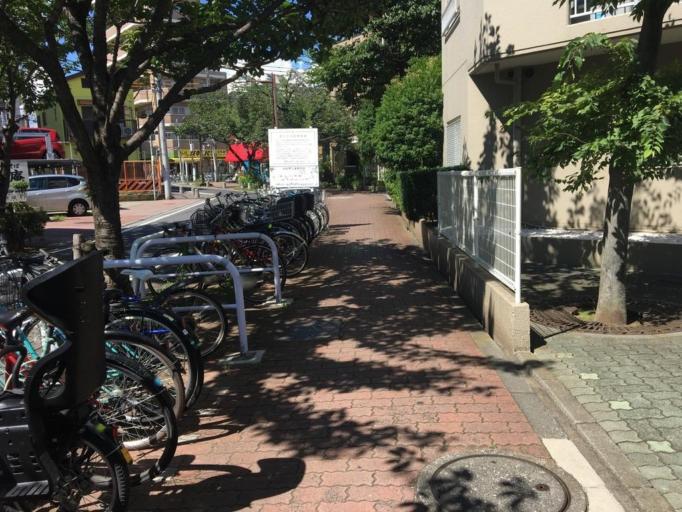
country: JP
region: Chiba
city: Matsudo
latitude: 35.7361
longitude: 139.8463
